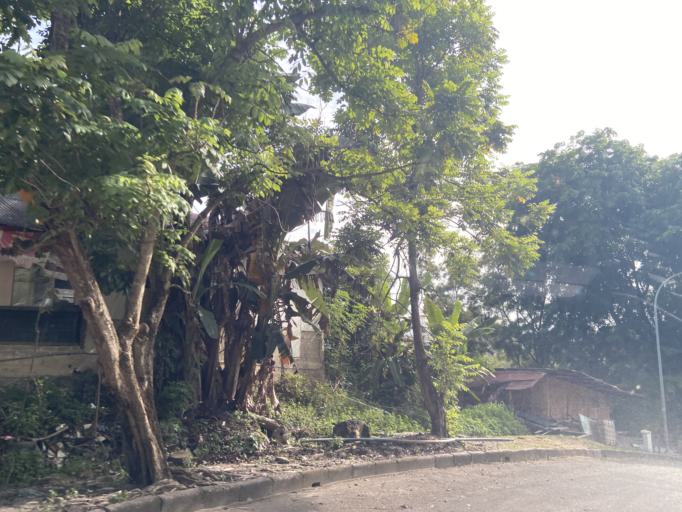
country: SG
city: Singapore
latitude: 1.1119
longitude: 104.0202
